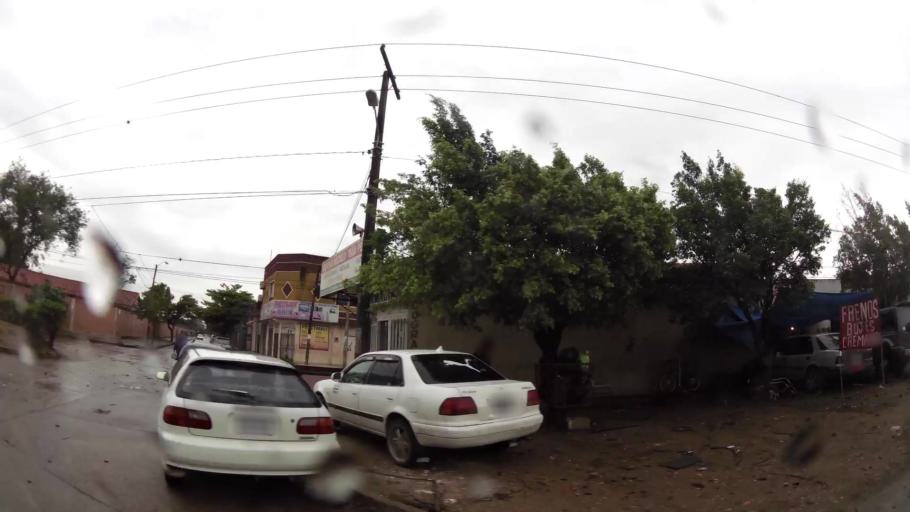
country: BO
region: Santa Cruz
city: Santa Cruz de la Sierra
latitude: -17.8121
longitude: -63.1917
